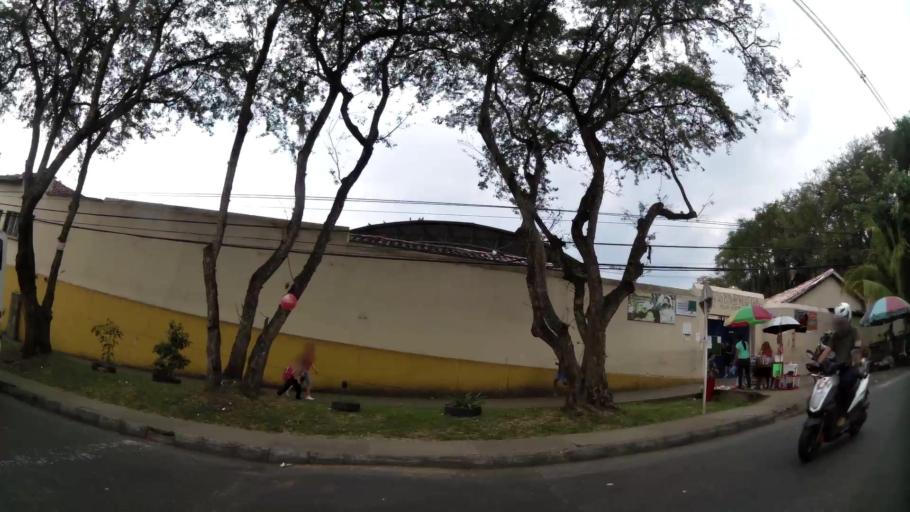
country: CO
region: Antioquia
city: Medellin
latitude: 6.2497
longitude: -75.5489
